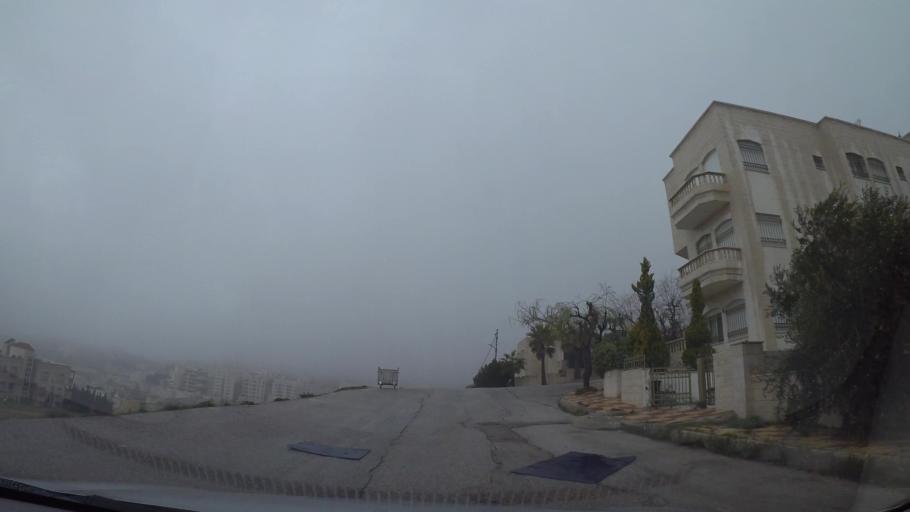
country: JO
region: Amman
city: Al Jubayhah
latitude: 32.0137
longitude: 35.8366
